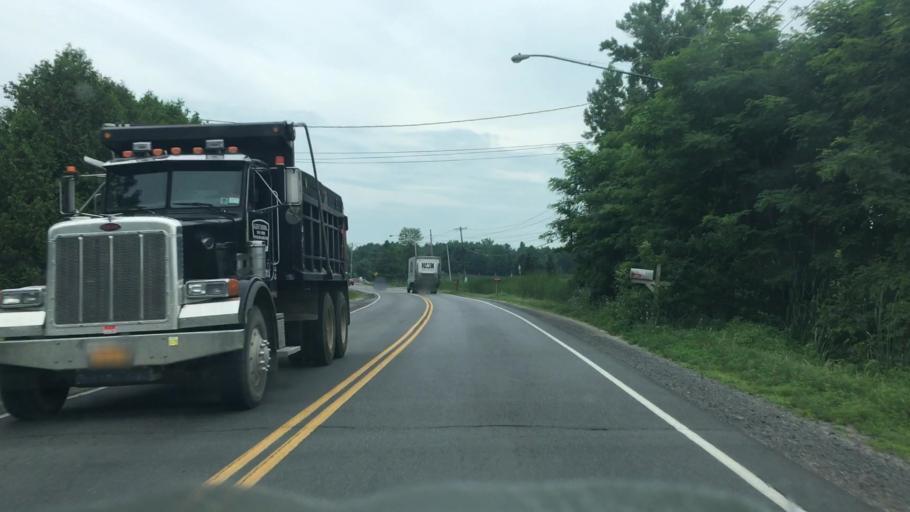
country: US
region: New York
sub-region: Clinton County
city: Plattsburgh West
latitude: 44.6716
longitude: -73.5072
